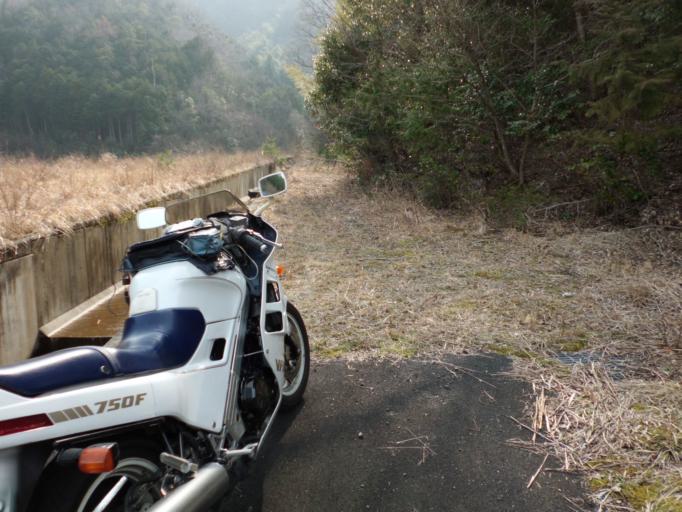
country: JP
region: Kyoto
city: Miyazu
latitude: 35.4413
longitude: 135.1748
